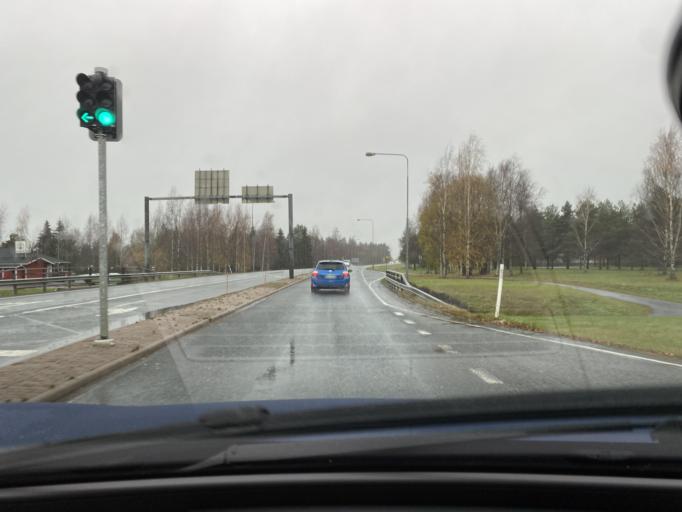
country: FI
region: Varsinais-Suomi
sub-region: Loimaa
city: Loimaa
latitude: 60.8602
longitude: 23.0276
